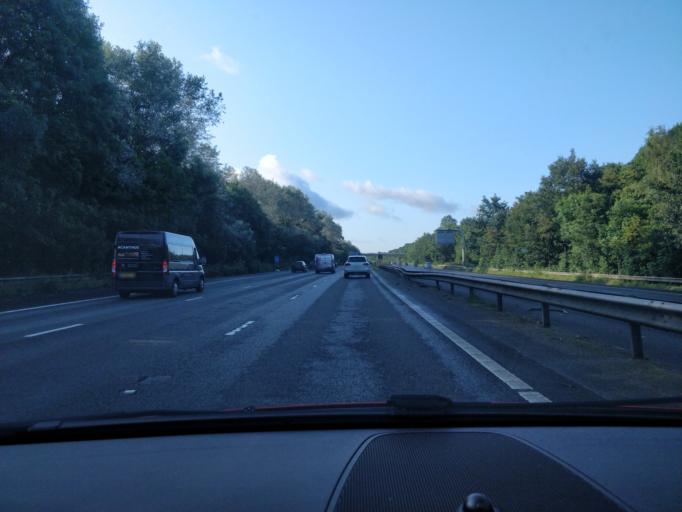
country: GB
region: England
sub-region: Knowsley
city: Knowsley
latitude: 53.4444
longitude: -2.8593
